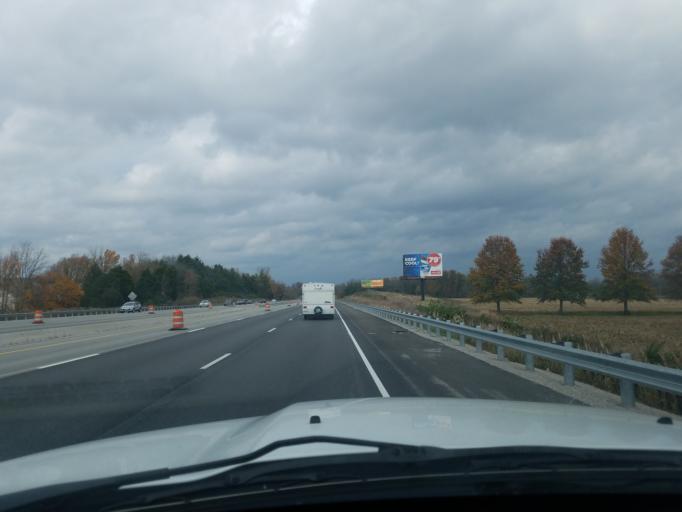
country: US
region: Indiana
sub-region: Clark County
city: Sellersburg
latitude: 38.4436
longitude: -85.7668
